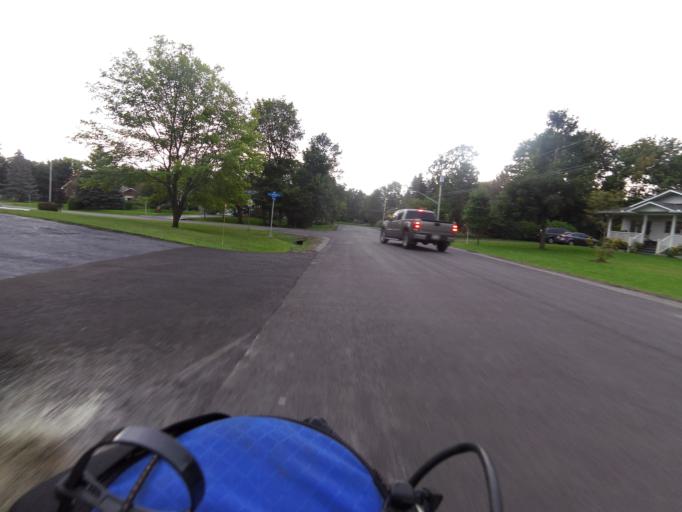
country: CA
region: Ontario
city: Ottawa
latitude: 45.2367
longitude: -75.4663
